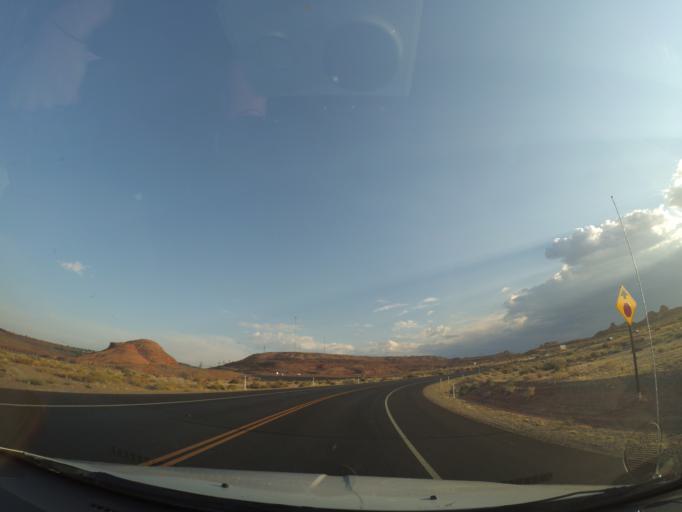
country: US
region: Arizona
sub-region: Coconino County
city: Page
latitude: 36.9410
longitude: -111.4935
